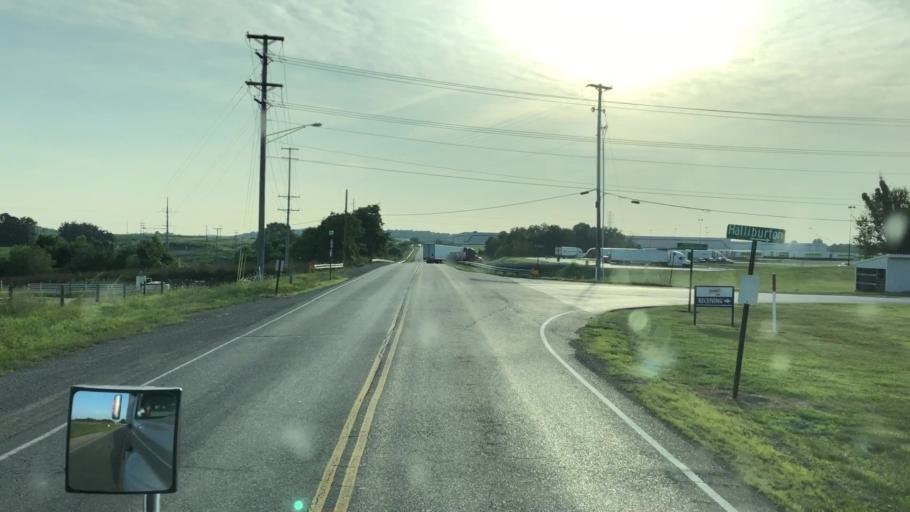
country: US
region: Ohio
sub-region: Muskingum County
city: Pleasant Grove
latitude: 39.9839
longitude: -81.9454
